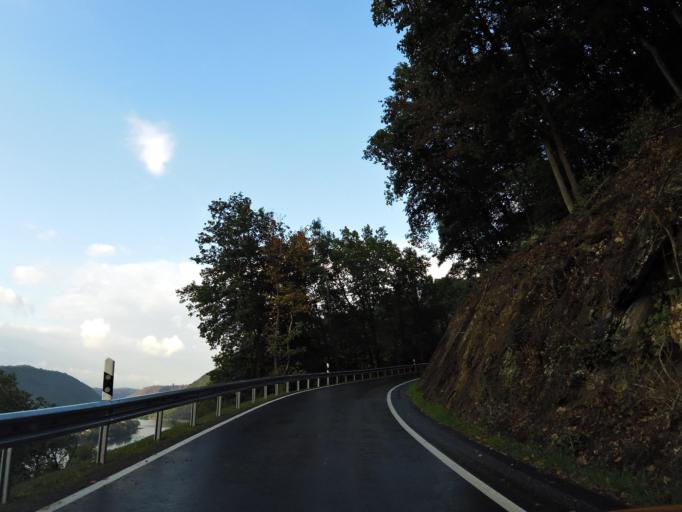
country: DE
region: Rheinland-Pfalz
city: Brodenbach
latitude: 50.2235
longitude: 7.4450
